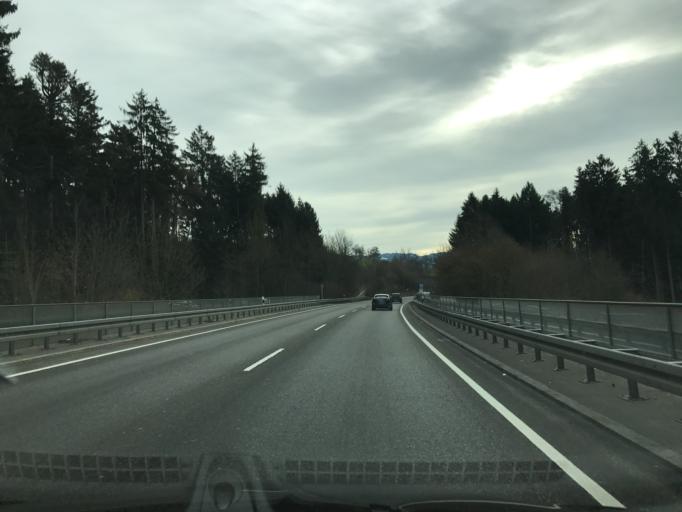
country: DE
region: Bavaria
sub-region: Swabia
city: Bodolz
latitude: 47.5788
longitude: 9.6835
